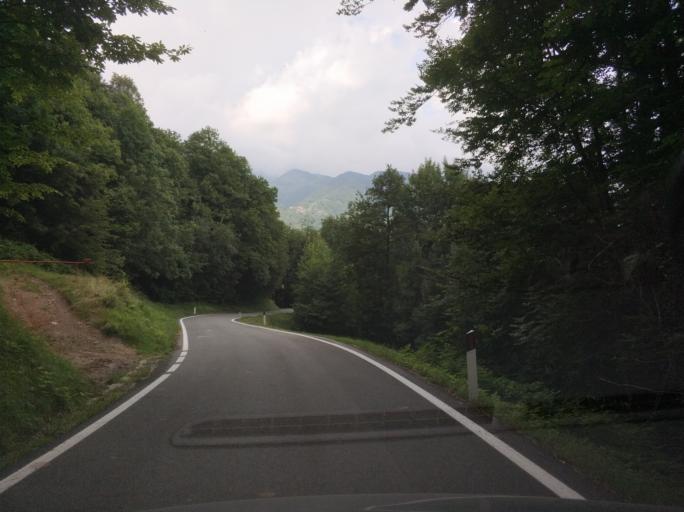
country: IT
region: Piedmont
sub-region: Provincia di Torino
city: Viu
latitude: 45.2259
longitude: 7.3780
